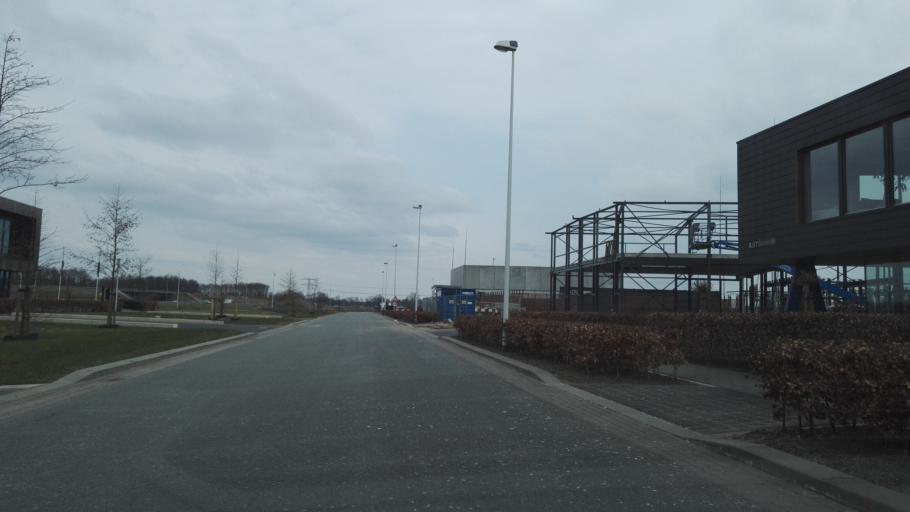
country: NL
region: Gelderland
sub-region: Gemeente Apeldoorn
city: Apeldoorn
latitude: 52.2468
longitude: 6.0016
